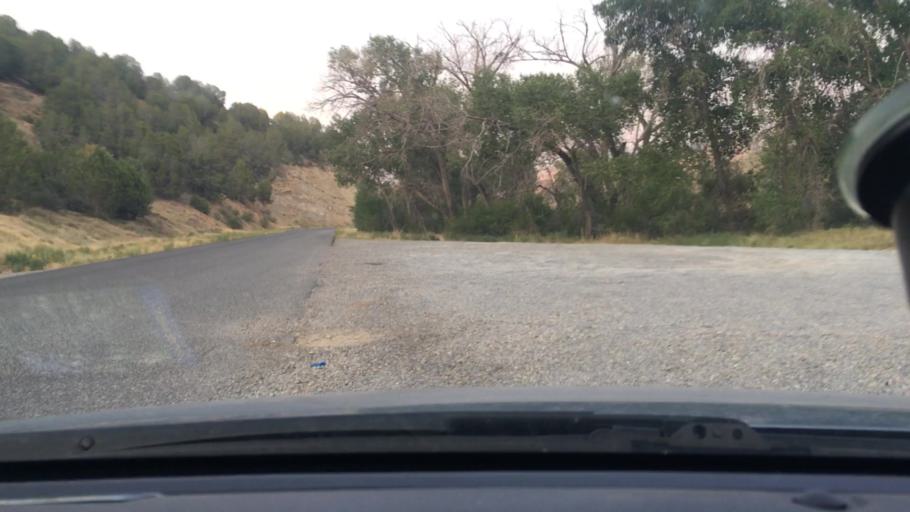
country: US
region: Utah
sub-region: Utah County
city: Mapleton
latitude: 40.0567
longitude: -111.4581
